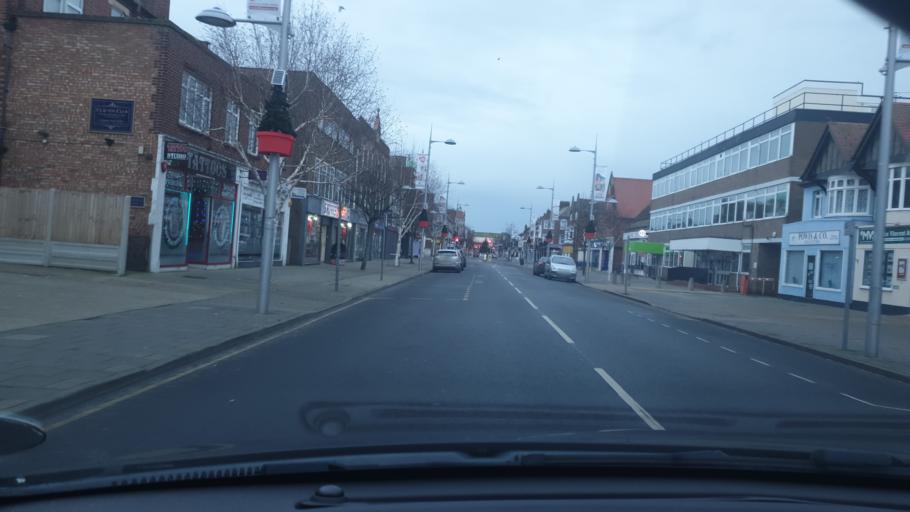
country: GB
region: England
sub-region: Essex
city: Clacton-on-Sea
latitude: 51.7910
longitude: 1.1538
